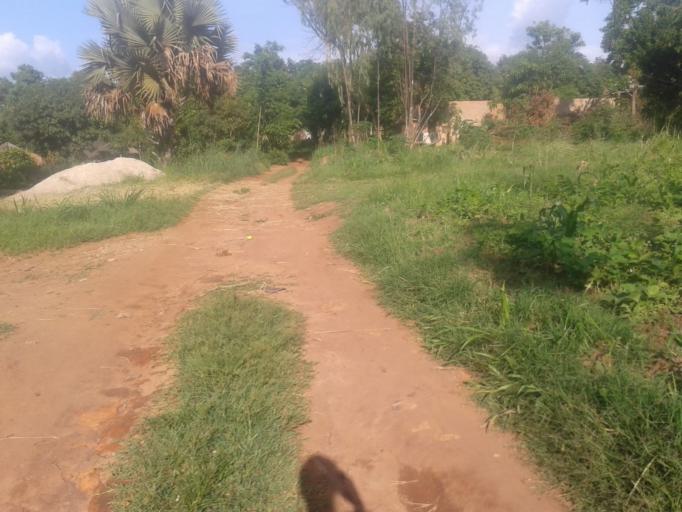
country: UG
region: Northern Region
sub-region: Gulu District
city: Gulu
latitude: 2.7897
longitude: 32.3138
